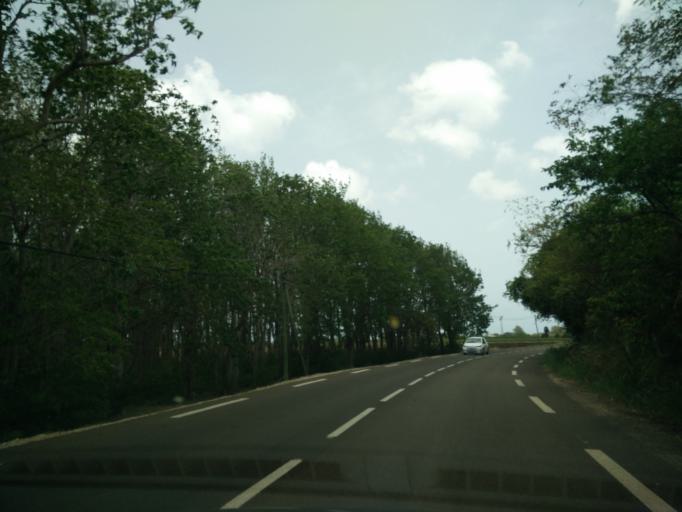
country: GP
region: Guadeloupe
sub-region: Guadeloupe
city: Anse-Bertrand
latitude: 16.4606
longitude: -61.5114
